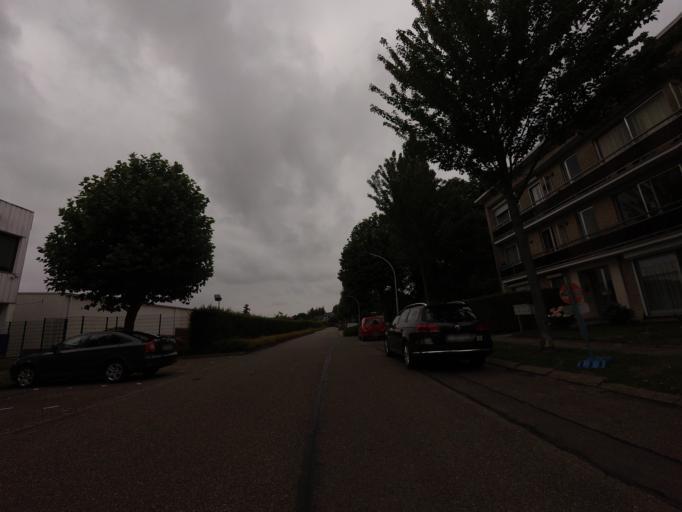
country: BE
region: Flanders
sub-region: Provincie Antwerpen
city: Edegem
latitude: 51.1531
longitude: 4.4406
